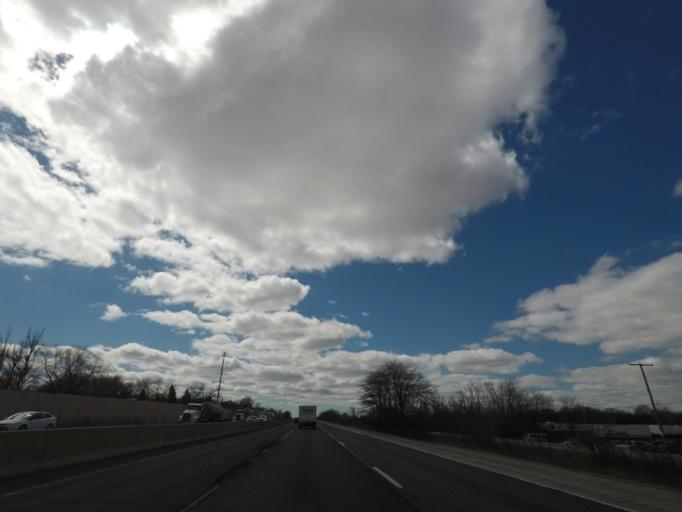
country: US
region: Illinois
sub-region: Will County
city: Crystal Lawns
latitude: 41.5538
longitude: -88.1806
